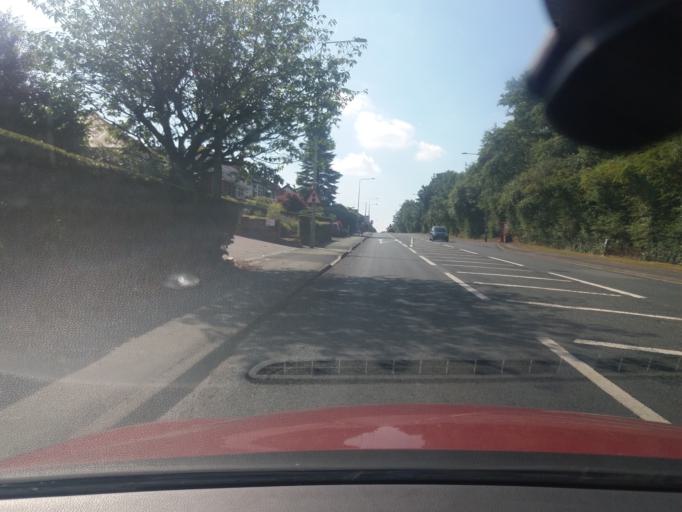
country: GB
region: England
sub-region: Lancashire
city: Chorley
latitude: 53.6349
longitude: -2.6145
